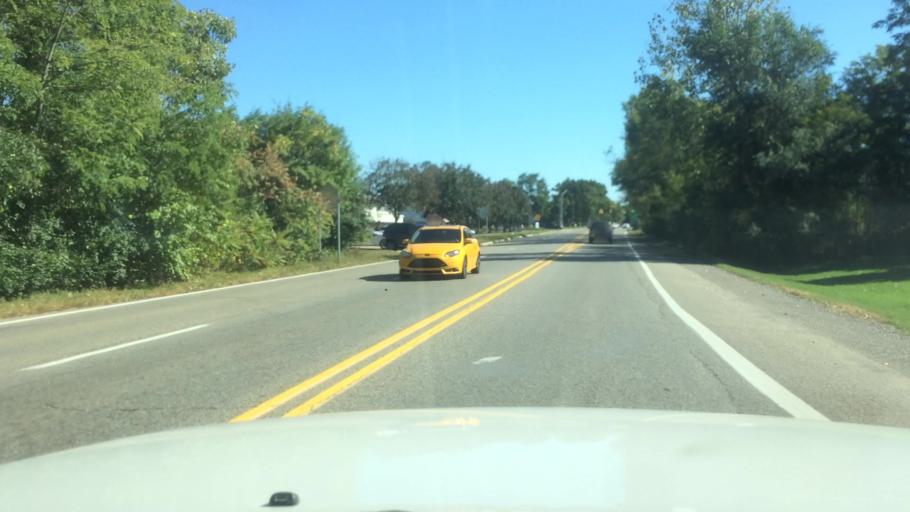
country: US
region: Michigan
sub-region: Oakland County
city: Wolverine Lake
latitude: 42.5778
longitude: -83.4498
